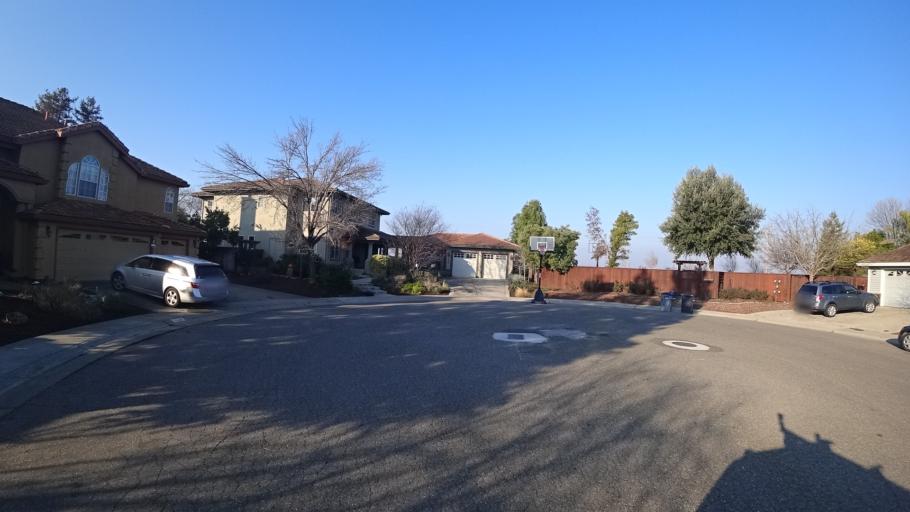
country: US
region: California
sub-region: Yolo County
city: Davis
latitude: 38.5595
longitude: -121.7932
